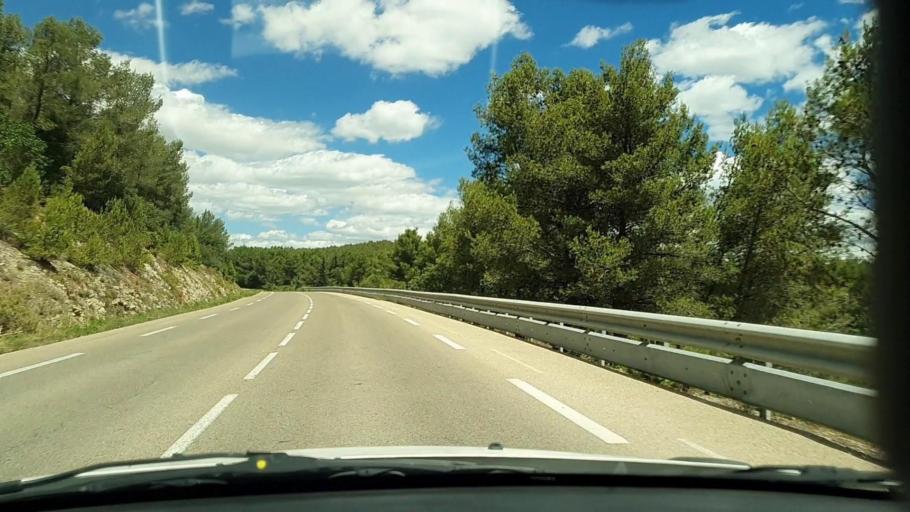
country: FR
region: Languedoc-Roussillon
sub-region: Departement du Gard
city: Poulx
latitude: 43.8798
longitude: 4.4172
